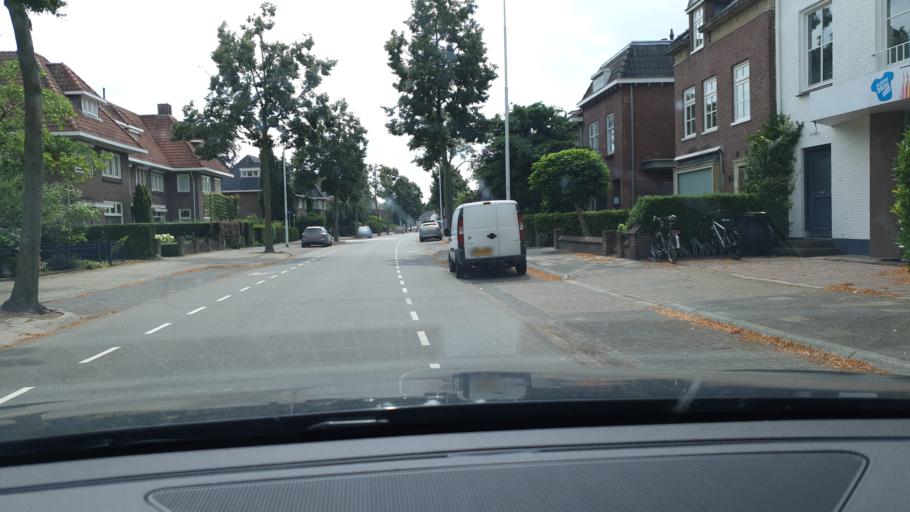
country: NL
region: North Brabant
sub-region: Gemeente Eindhoven
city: Eindhoven
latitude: 51.4300
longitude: 5.4714
